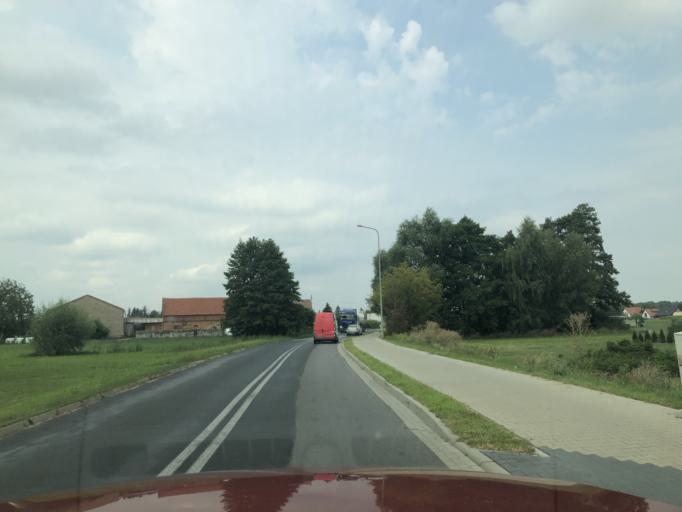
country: PL
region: Greater Poland Voivodeship
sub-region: Powiat leszczynski
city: Wloszakowice
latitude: 51.8902
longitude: 16.4072
